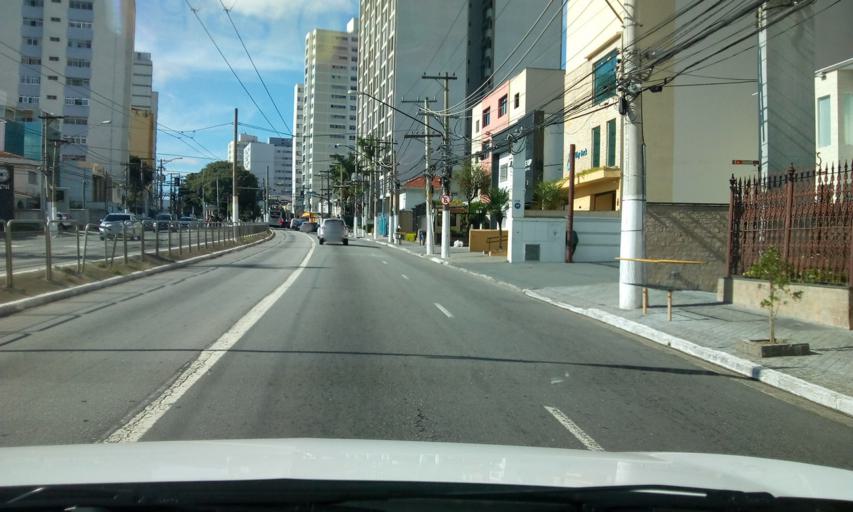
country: BR
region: Sao Paulo
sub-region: Sao Paulo
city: Sao Paulo
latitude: -23.5644
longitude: -46.5965
